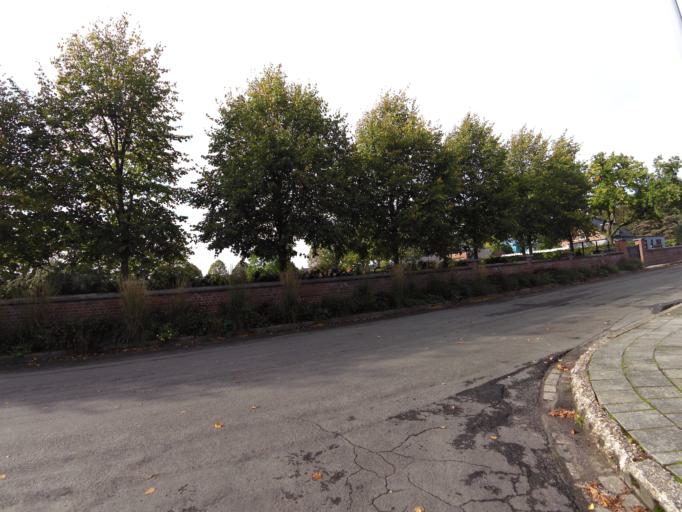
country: BE
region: Flanders
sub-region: Provincie West-Vlaanderen
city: Brugge
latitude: 51.1883
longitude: 3.2165
